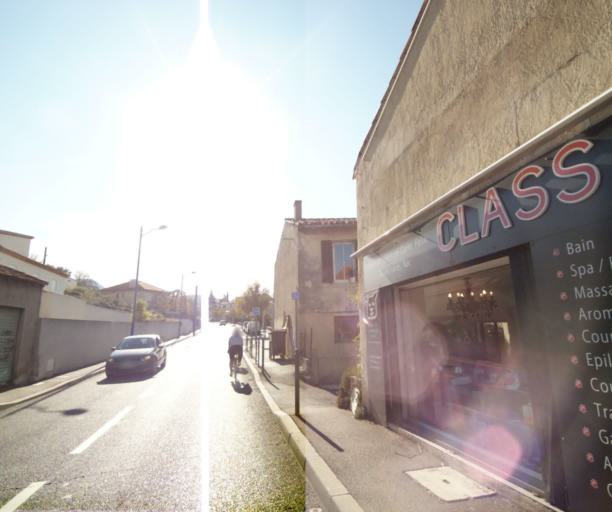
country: FR
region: Provence-Alpes-Cote d'Azur
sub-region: Departement des Bouches-du-Rhone
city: Allauch
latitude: 43.3557
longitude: 5.4869
